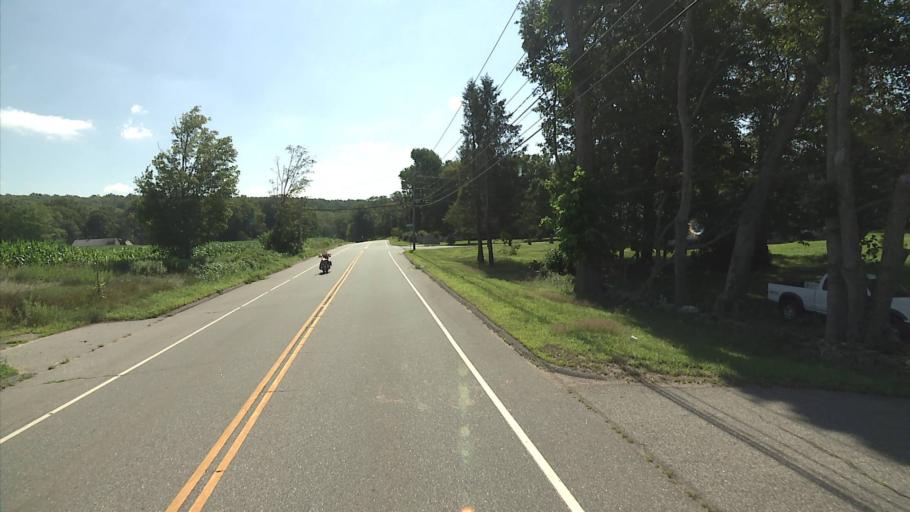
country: US
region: Connecticut
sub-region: Windham County
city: Windham
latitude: 41.7101
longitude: -72.1704
